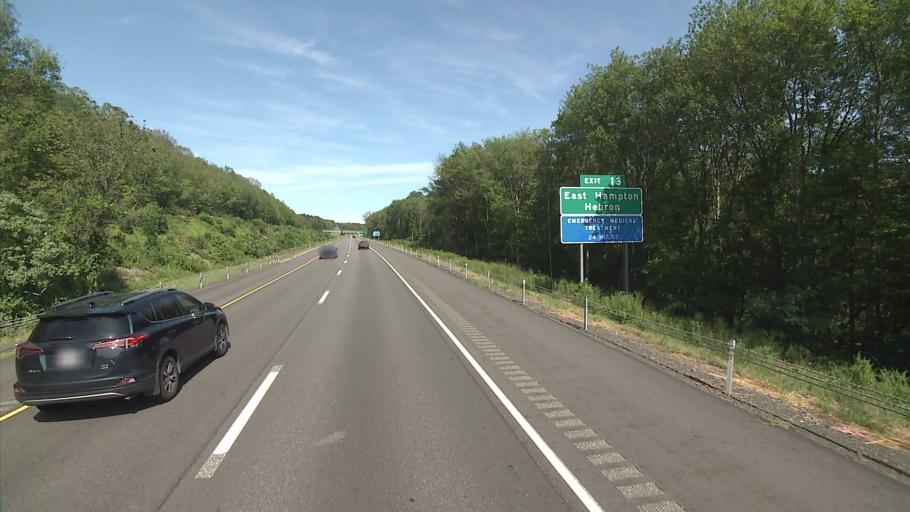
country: US
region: Connecticut
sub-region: Hartford County
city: Terramuggus
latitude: 41.6271
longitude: -72.4438
